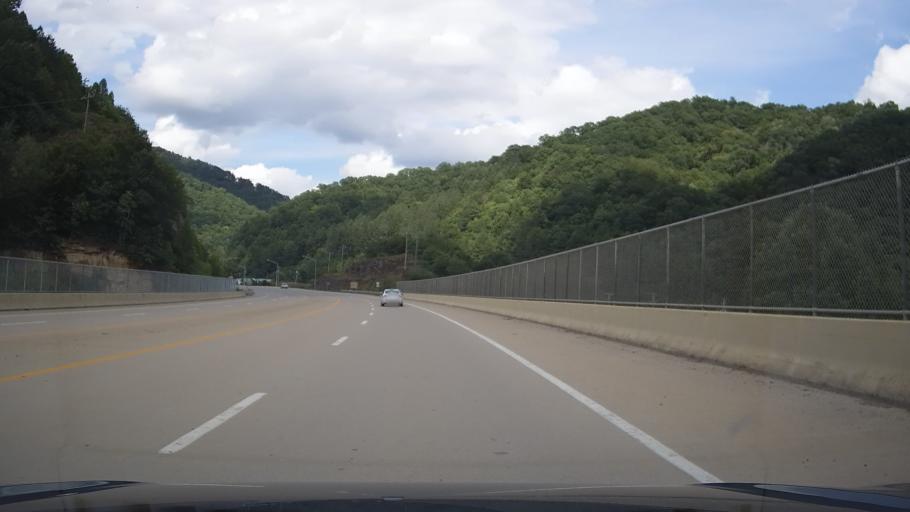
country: US
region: Kentucky
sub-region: Letcher County
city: Jenkins
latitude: 37.2781
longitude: -82.5812
